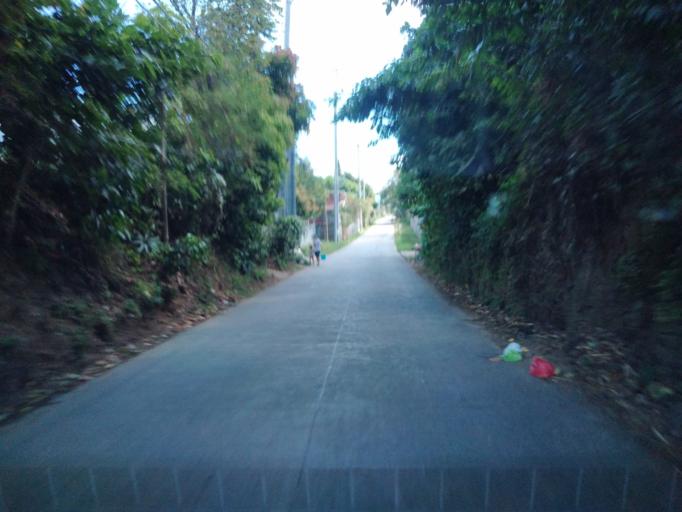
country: PH
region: Central Luzon
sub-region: Province of Bulacan
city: Balasing
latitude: 14.8493
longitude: 120.9973
